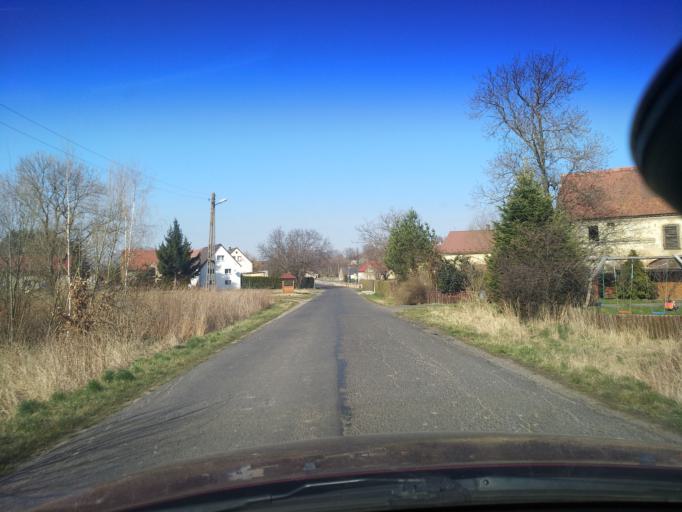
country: PL
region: Lower Silesian Voivodeship
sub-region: Powiat zgorzelecki
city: Sulikow
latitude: 51.0563
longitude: 15.1085
